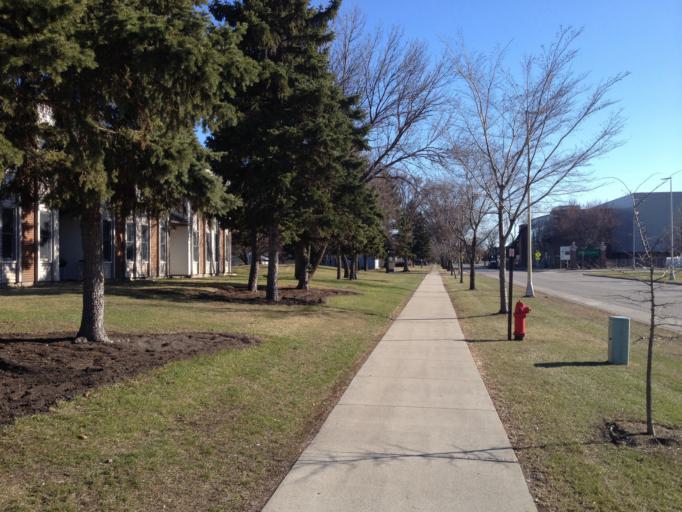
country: US
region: North Dakota
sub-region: Cass County
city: Fargo
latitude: 46.9021
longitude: -96.7979
